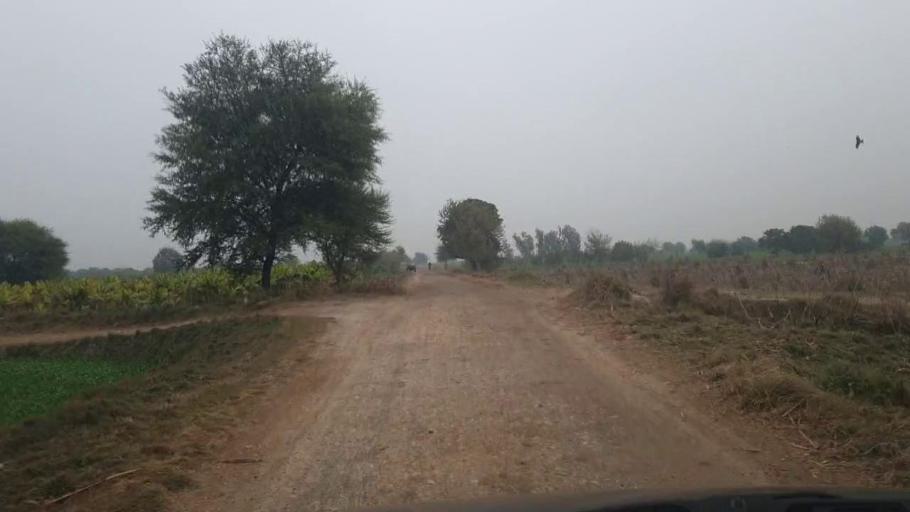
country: PK
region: Sindh
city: Tando Adam
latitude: 25.8028
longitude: 68.6762
